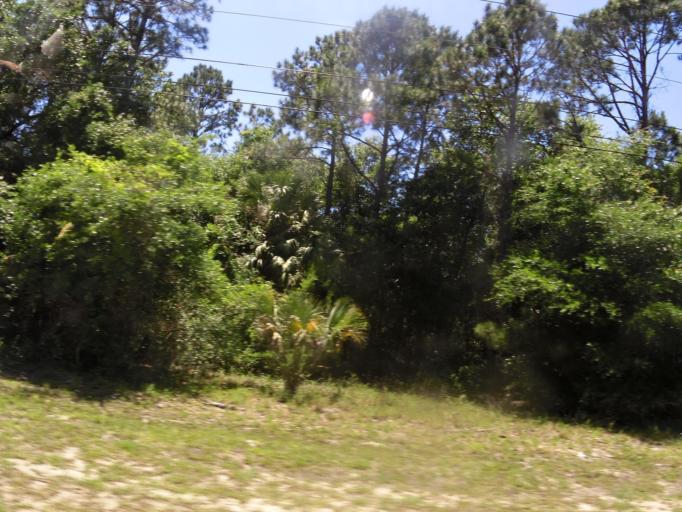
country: US
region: Florida
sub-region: Flagler County
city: Flagler Beach
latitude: 29.4504
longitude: -81.1646
